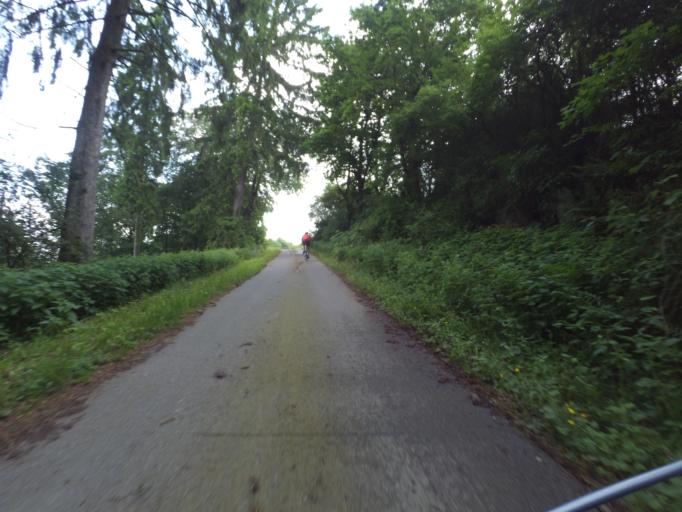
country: DE
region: Rheinland-Pfalz
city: Buch
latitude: 50.0528
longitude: 7.3815
